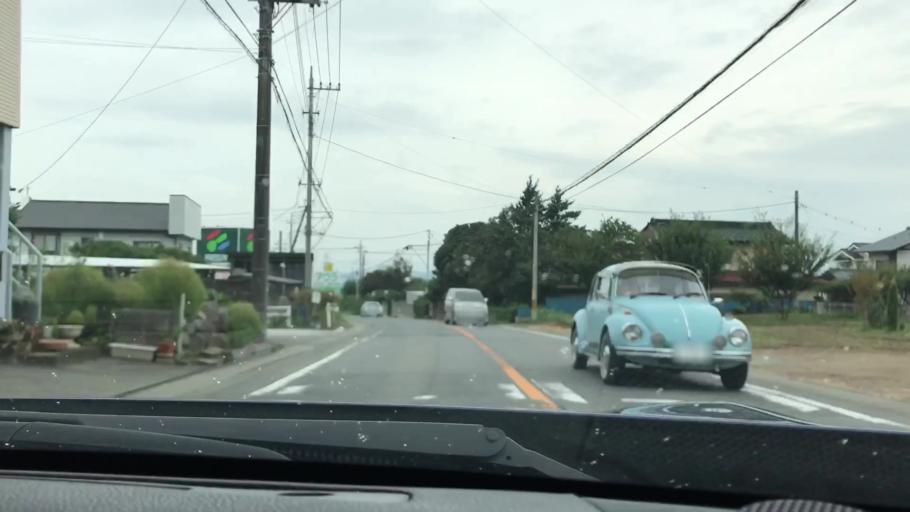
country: JP
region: Gunma
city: Kanekomachi
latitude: 36.3931
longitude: 138.9604
